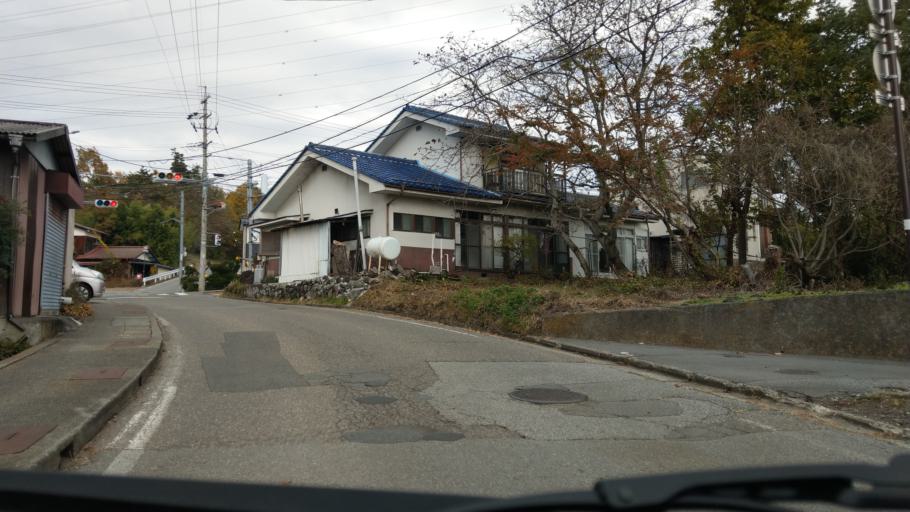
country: JP
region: Nagano
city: Komoro
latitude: 36.3202
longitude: 138.4424
